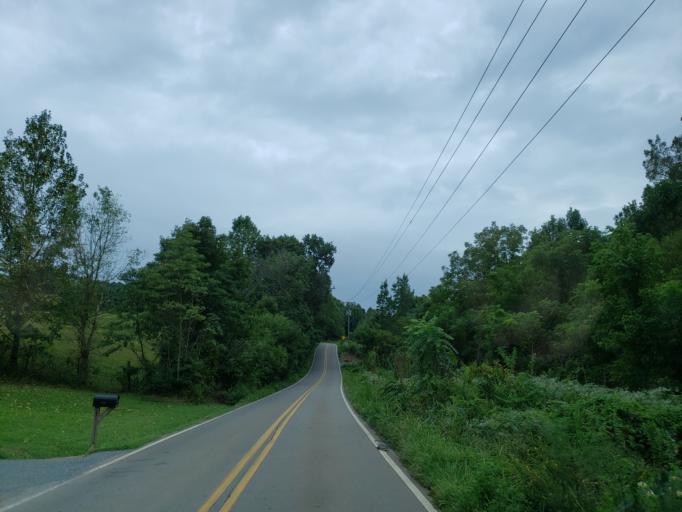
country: US
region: Georgia
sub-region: Pickens County
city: Jasper
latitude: 34.4278
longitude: -84.5472
